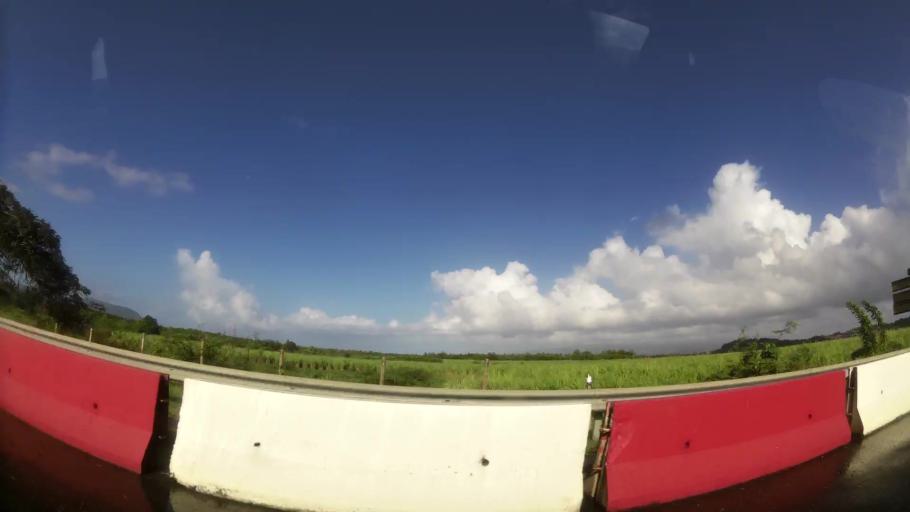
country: MQ
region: Martinique
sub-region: Martinique
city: Ducos
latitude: 14.5437
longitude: -60.9759
